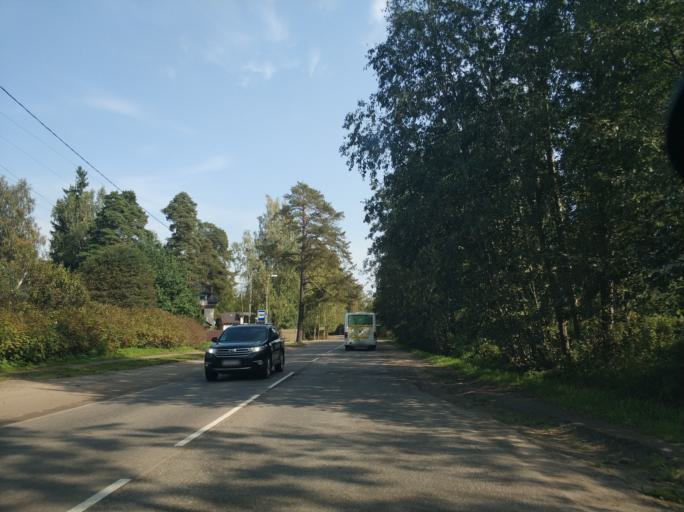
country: RU
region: Leningrad
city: Vsevolozhsk
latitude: 60.0097
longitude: 30.6155
